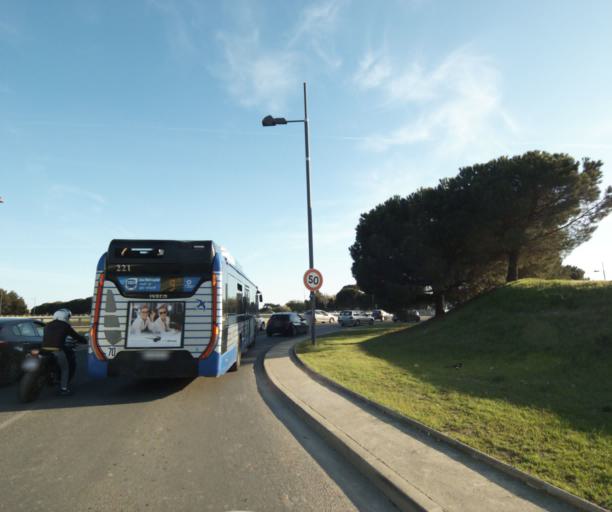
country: FR
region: Languedoc-Roussillon
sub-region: Departement de l'Herault
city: Castelnau-le-Lez
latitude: 43.6089
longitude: 3.9297
